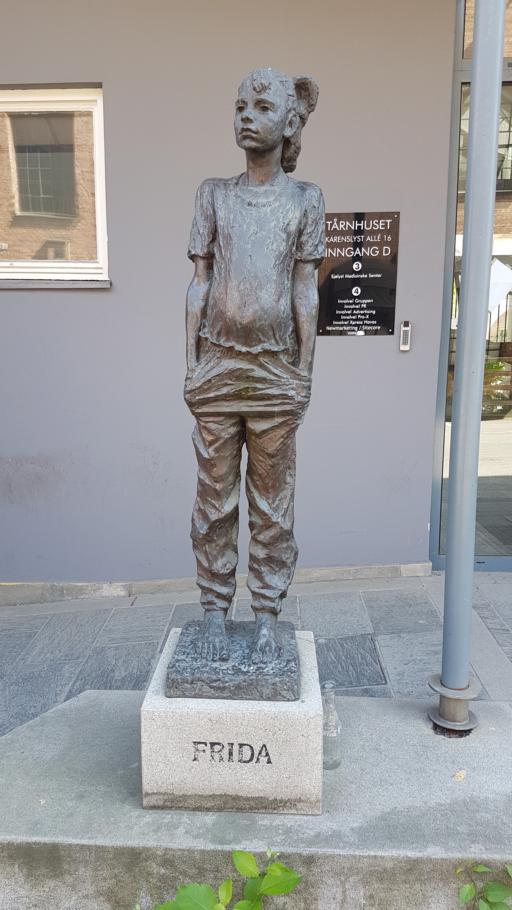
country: NO
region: Oslo
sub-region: Oslo
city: Sjolyststranda
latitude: 59.9194
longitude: 10.6839
